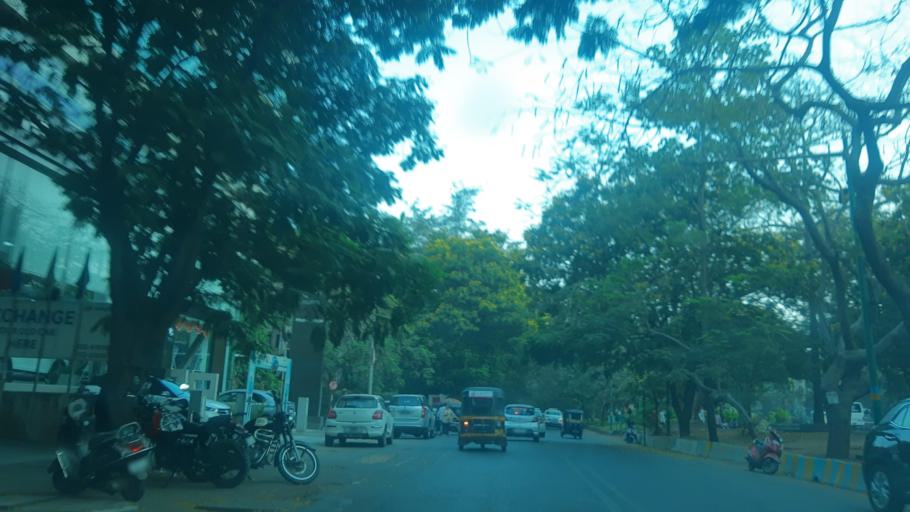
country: IN
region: Maharashtra
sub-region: Thane
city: Thane
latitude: 19.1935
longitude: 72.9632
